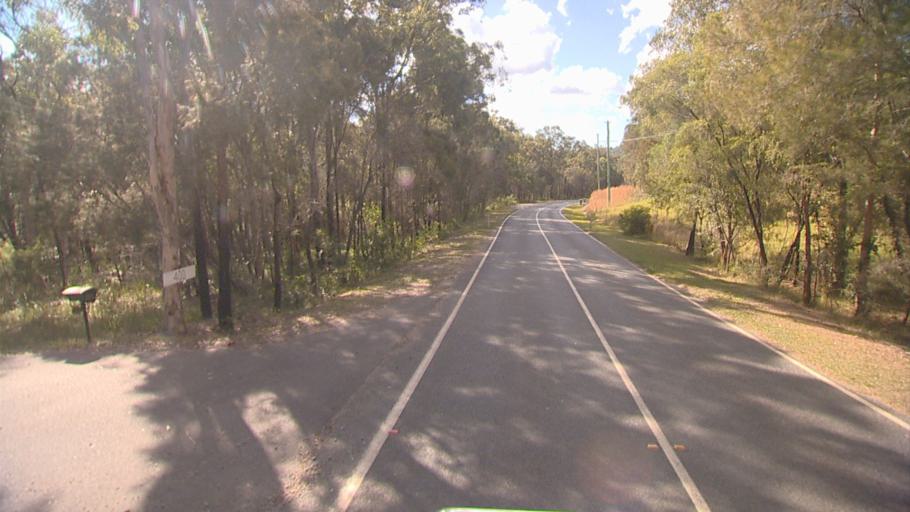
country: AU
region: Queensland
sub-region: Logan
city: Slacks Creek
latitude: -27.6417
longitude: 153.2068
